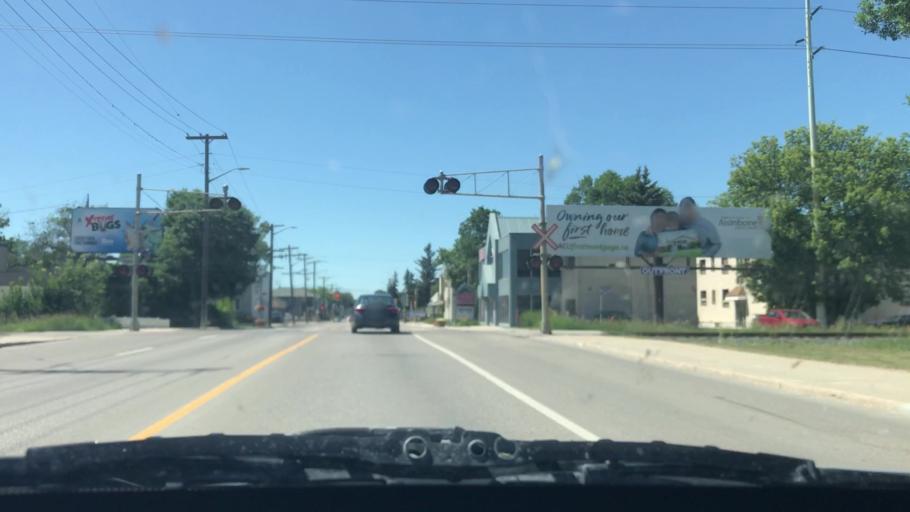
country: CA
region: Manitoba
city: Winnipeg
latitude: 49.8742
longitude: -97.1943
